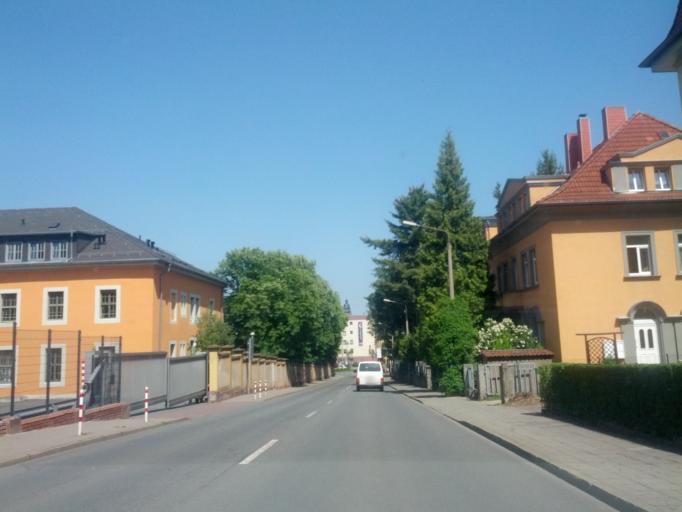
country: DE
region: Thuringia
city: Gotha
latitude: 50.9479
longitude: 10.6949
